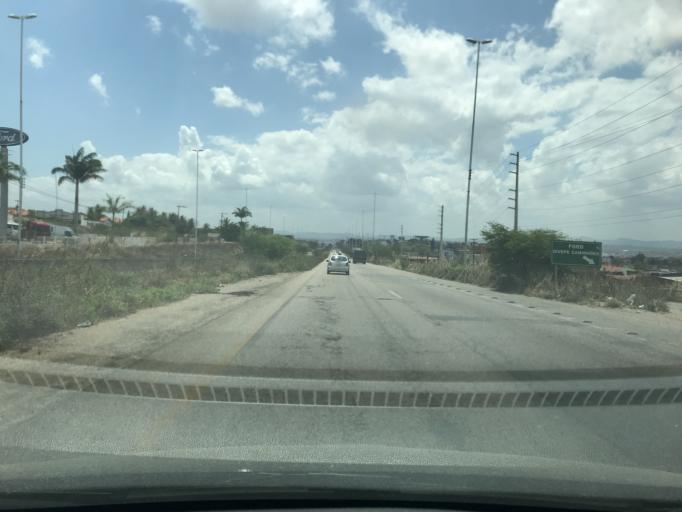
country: BR
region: Pernambuco
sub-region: Caruaru
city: Caruaru
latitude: -8.3052
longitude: -35.9681
